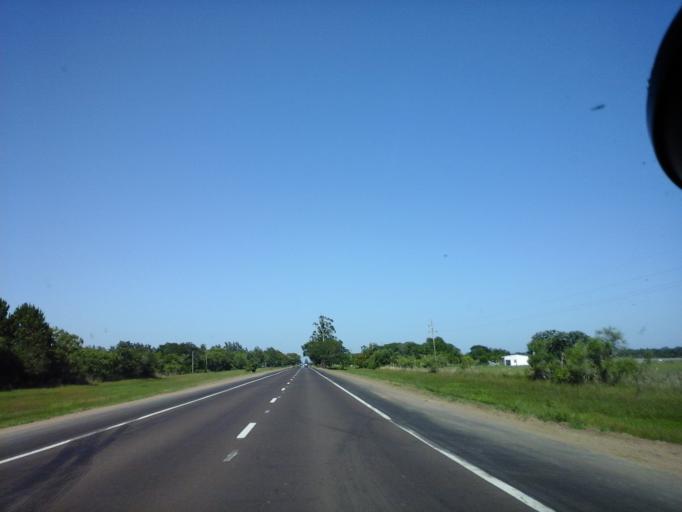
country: AR
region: Corrientes
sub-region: Departamento de Itati
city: Itati
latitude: -27.3667
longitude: -58.3374
